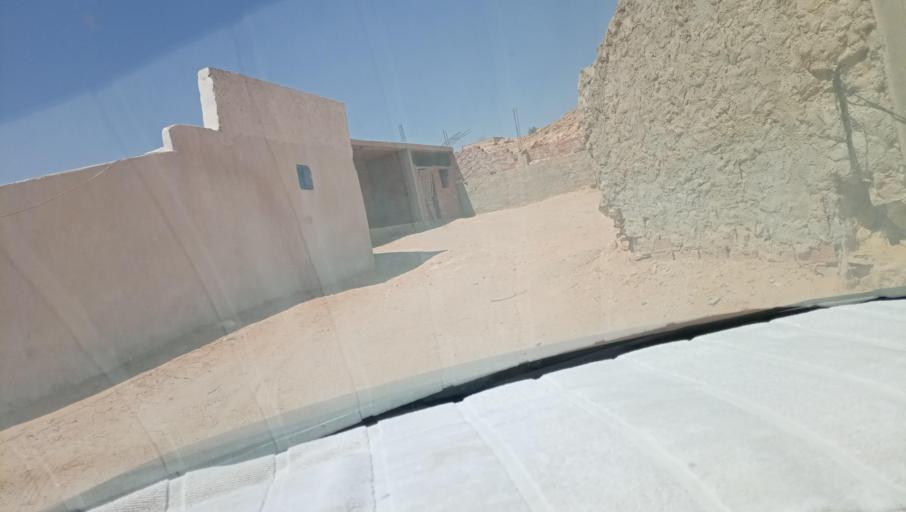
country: TN
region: Tataouine
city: Tataouine
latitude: 32.8578
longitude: 10.4736
